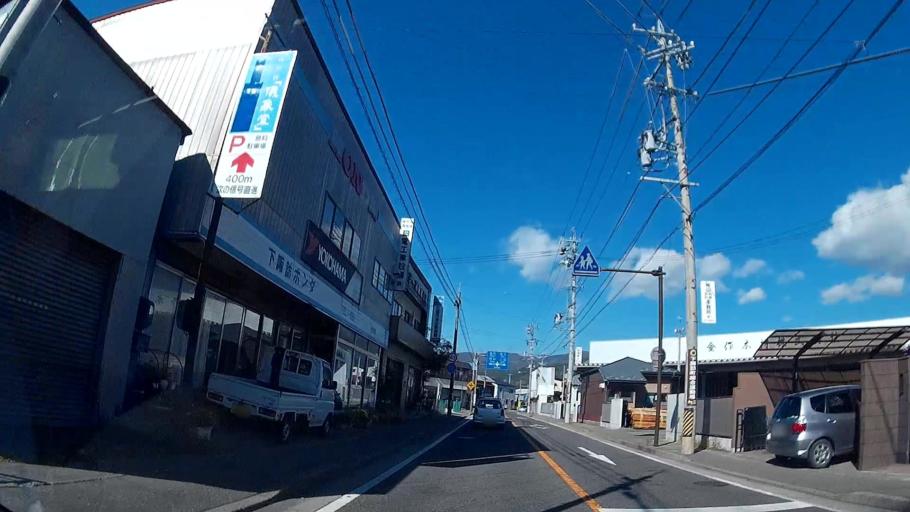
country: JP
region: Nagano
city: Suwa
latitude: 36.0723
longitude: 138.0878
